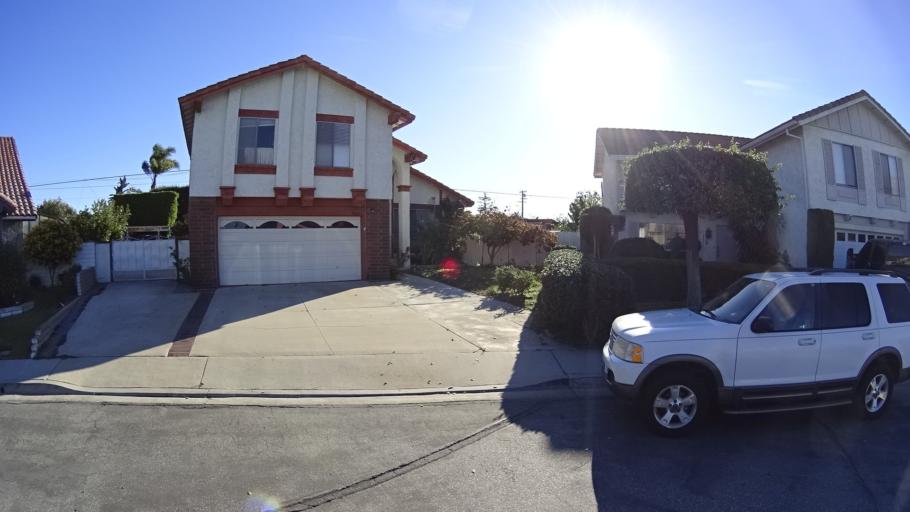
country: US
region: California
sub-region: Orange County
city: Garden Grove
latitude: 33.7700
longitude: -117.9642
